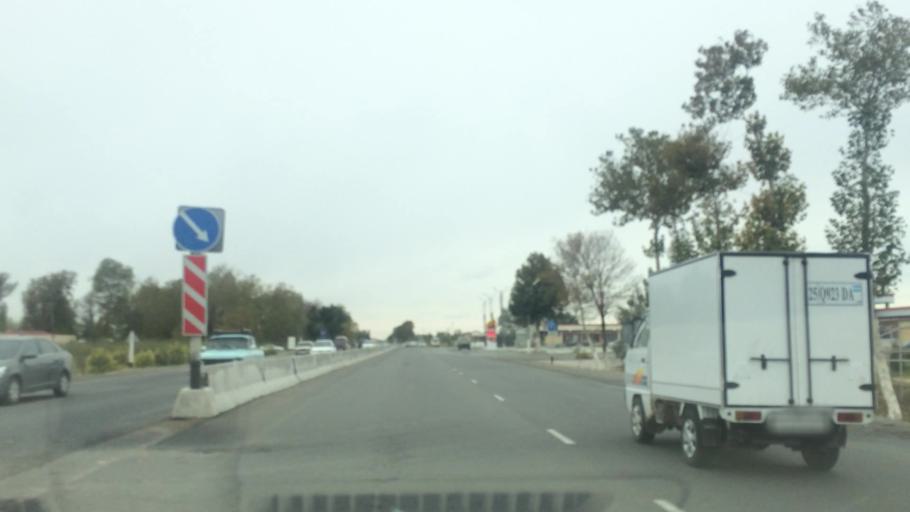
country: UZ
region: Samarqand
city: Jomboy
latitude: 39.7206
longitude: 67.1191
